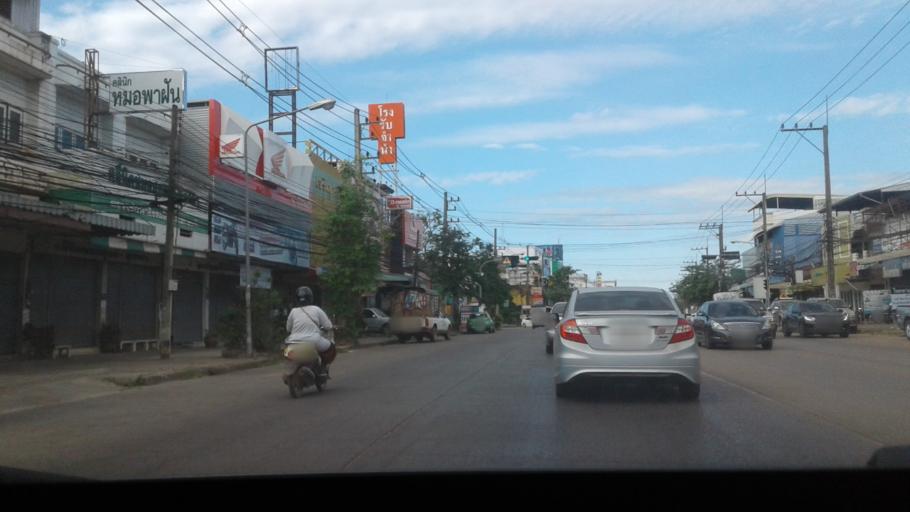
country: TH
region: Changwat Udon Thani
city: Udon Thani
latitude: 17.4243
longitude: 102.7907
